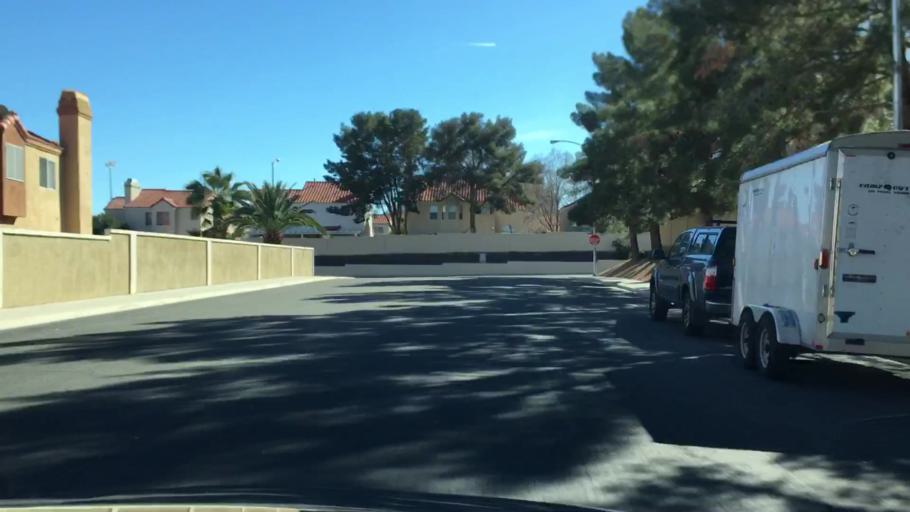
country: US
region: Nevada
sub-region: Clark County
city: Whitney
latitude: 36.0618
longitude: -115.0607
